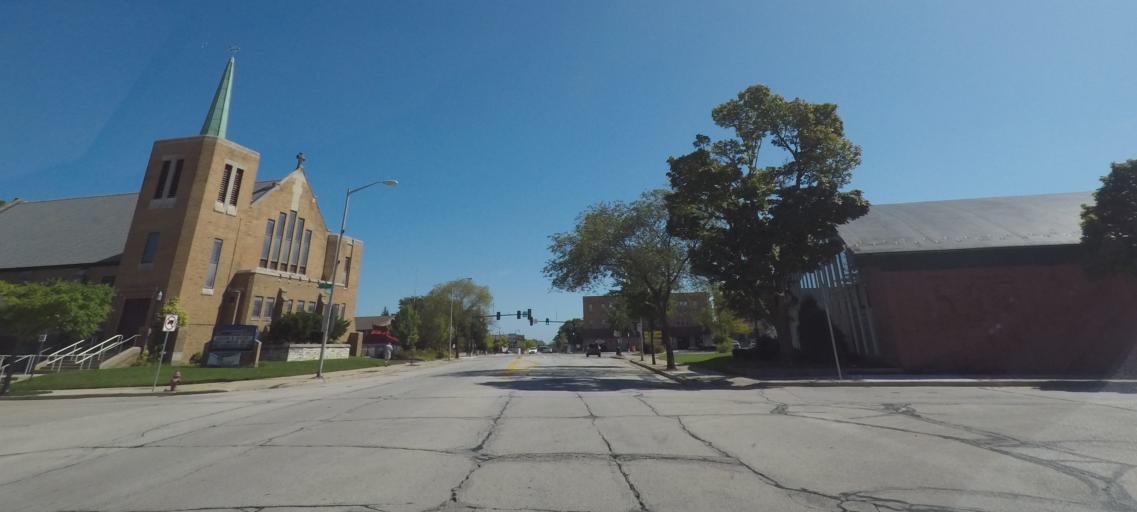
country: US
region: Wisconsin
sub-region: Milwaukee County
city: West Allis
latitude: 43.0115
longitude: -88.0086
